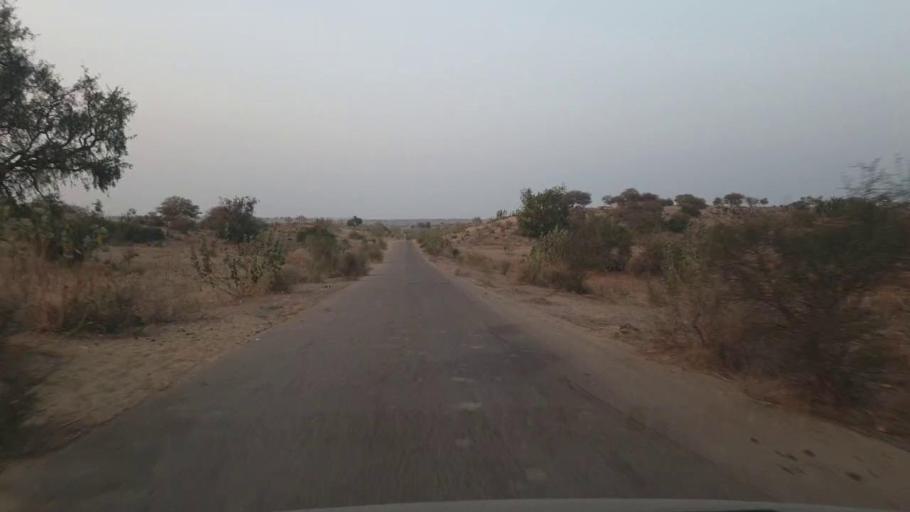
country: PK
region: Sindh
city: Umarkot
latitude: 25.3428
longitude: 70.0510
